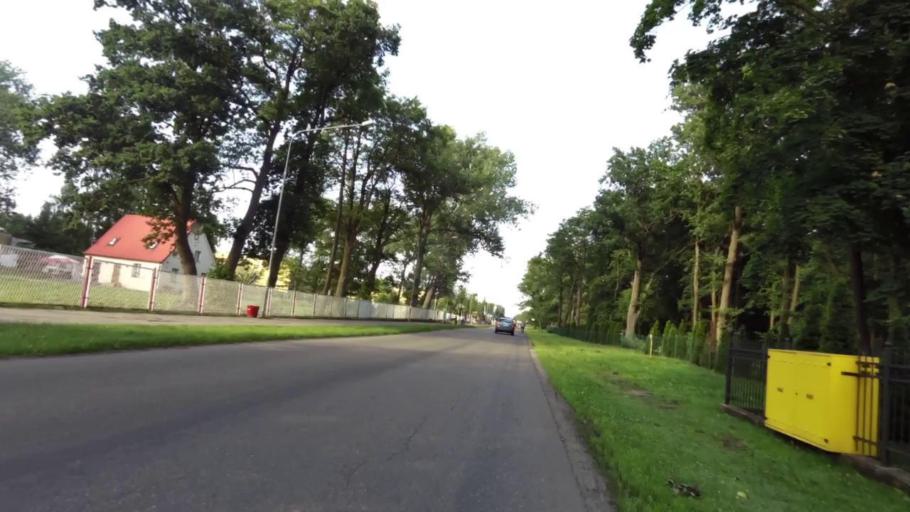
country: PL
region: West Pomeranian Voivodeship
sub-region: Powiat slawienski
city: Darlowo
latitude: 54.3835
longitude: 16.3213
